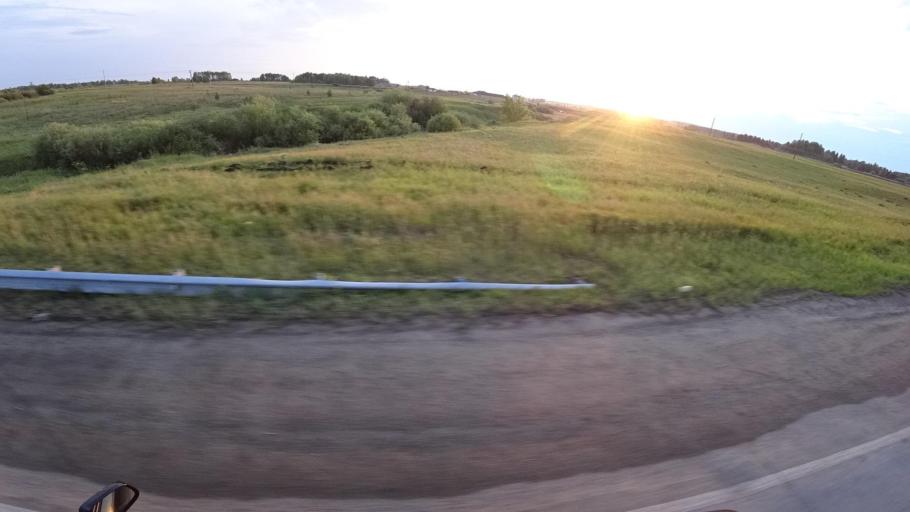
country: RU
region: Sverdlovsk
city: Kamyshlov
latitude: 56.8742
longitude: 62.7117
